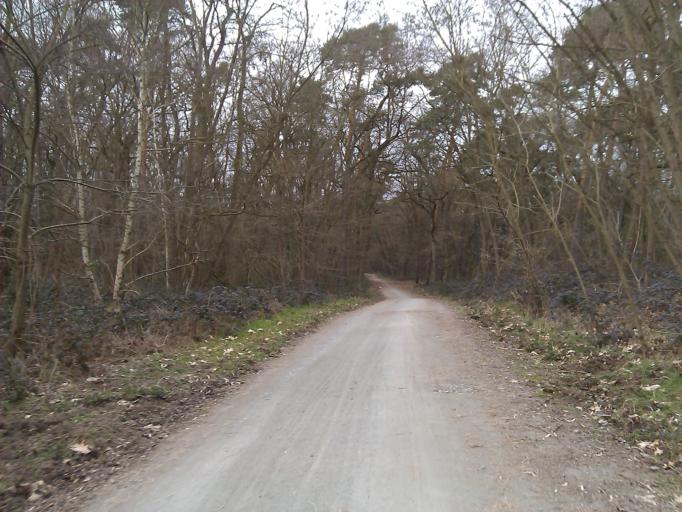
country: DE
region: Hesse
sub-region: Regierungsbezirk Darmstadt
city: Trebur
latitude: 49.9527
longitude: 8.4348
